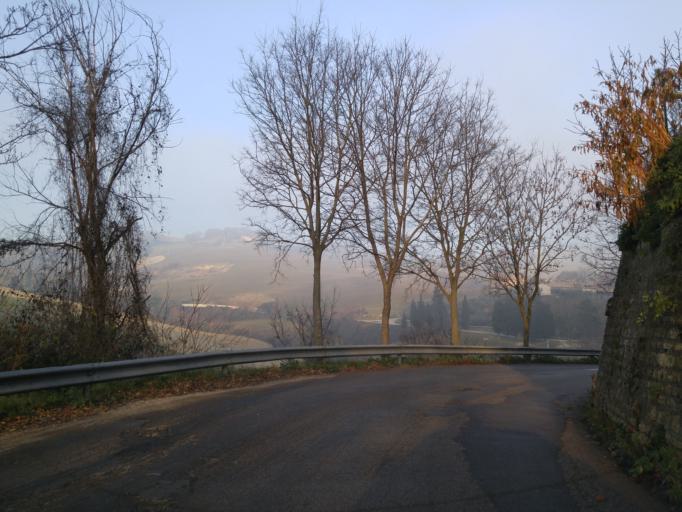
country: IT
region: The Marches
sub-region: Provincia di Pesaro e Urbino
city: Isola del Piano
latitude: 43.7381
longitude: 12.7828
